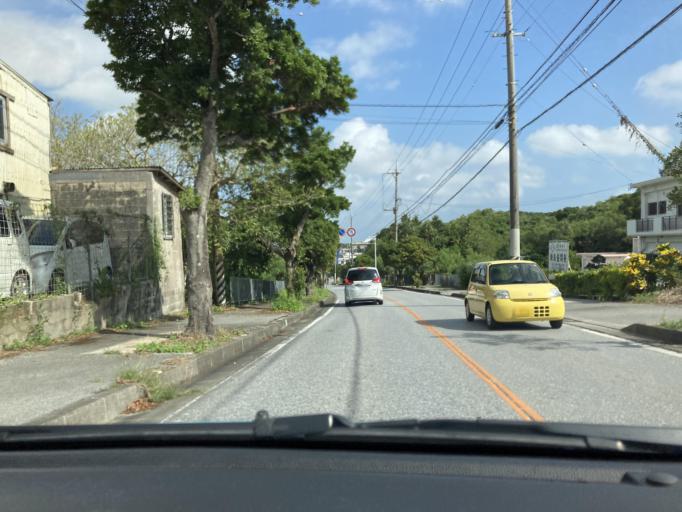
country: JP
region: Okinawa
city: Ginowan
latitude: 26.2582
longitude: 127.7765
